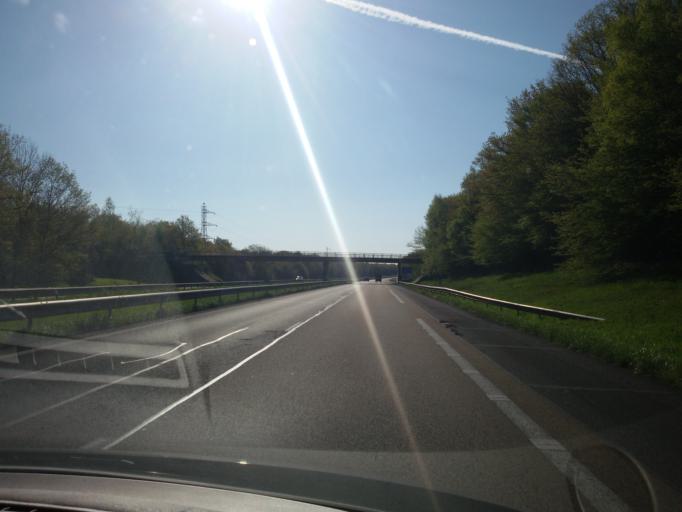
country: FR
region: Bourgogne
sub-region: Departement de l'Yonne
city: Cheroy
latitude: 48.1112
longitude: 3.0008
